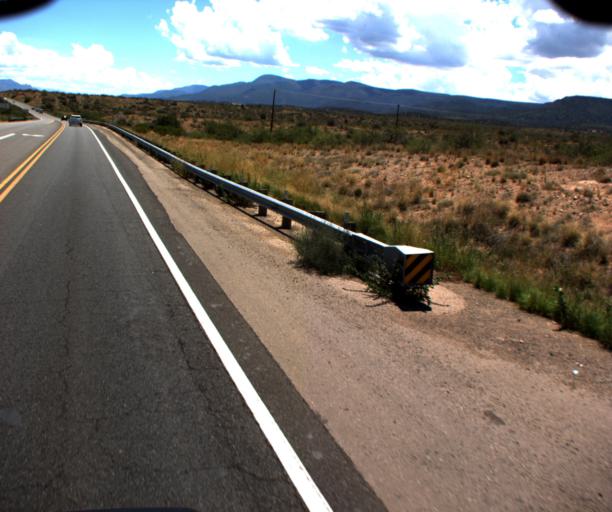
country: US
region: Arizona
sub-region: Yavapai County
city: Camp Verde
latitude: 34.6087
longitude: -111.9115
